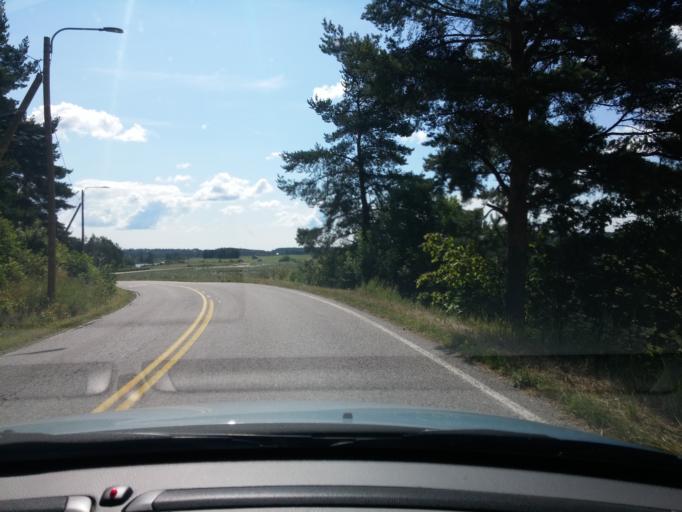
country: FI
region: Uusimaa
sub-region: Porvoo
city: Porvoo
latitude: 60.4178
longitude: 25.6125
